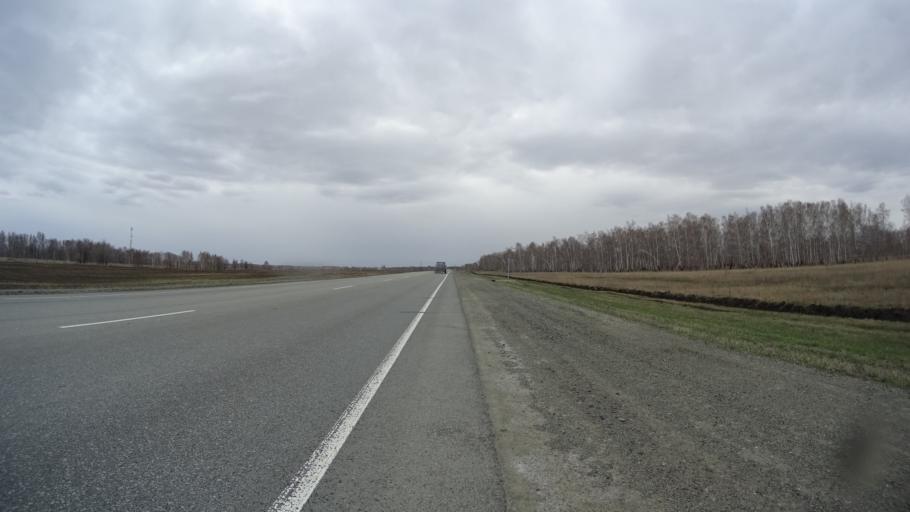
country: RU
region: Chelyabinsk
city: Krasnogorskiy
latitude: 54.6902
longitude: 61.2486
